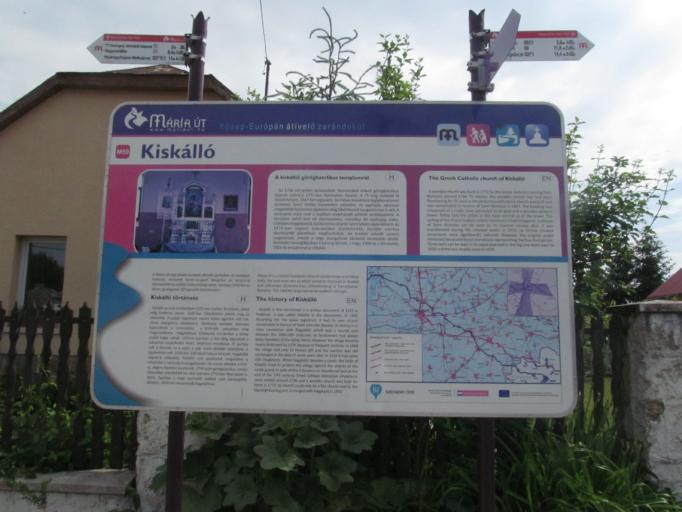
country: HU
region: Szabolcs-Szatmar-Bereg
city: Nagykallo
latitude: 47.8783
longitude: 21.8615
